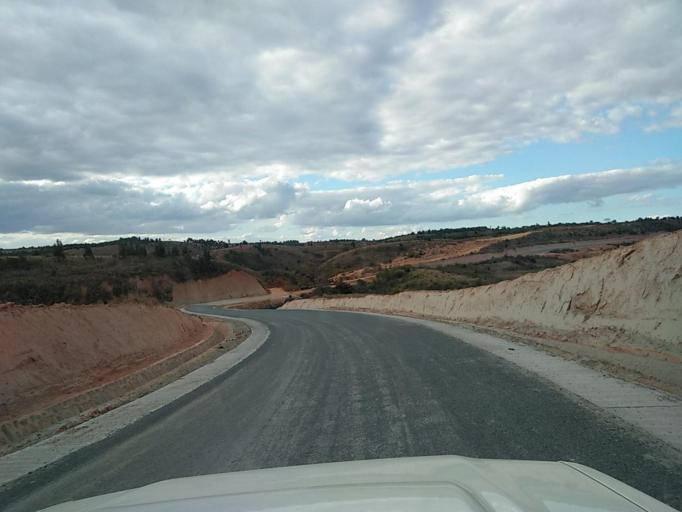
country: MG
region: Alaotra Mangoro
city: Ambatondrazaka
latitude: -18.0214
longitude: 48.2578
